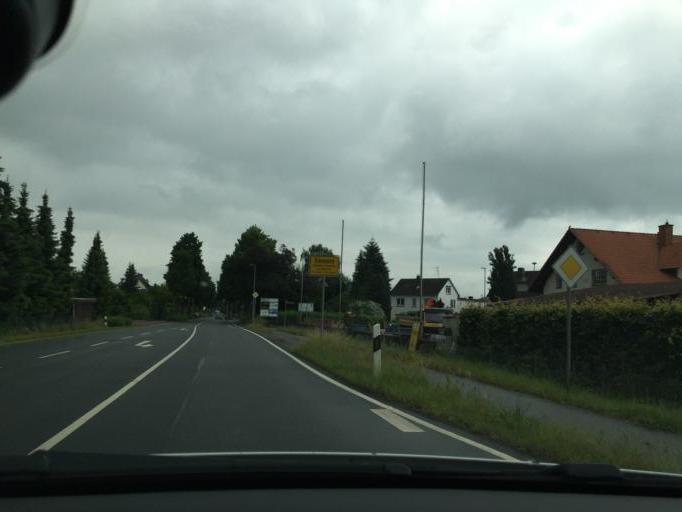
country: DE
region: Lower Saxony
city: Hameln
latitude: 52.0455
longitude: 9.3716
